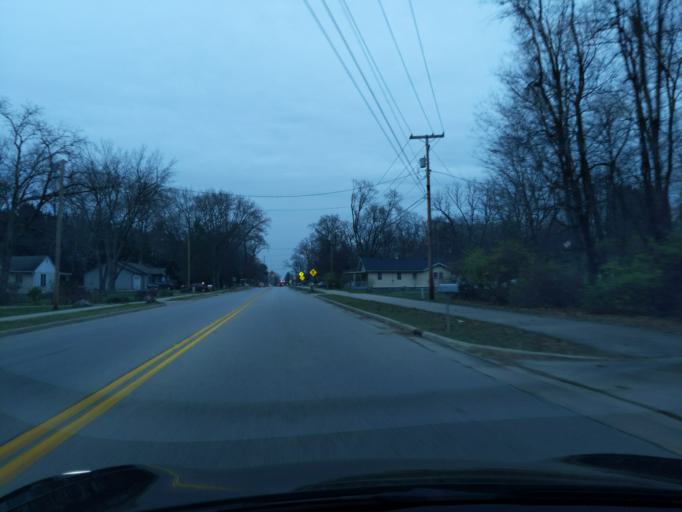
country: US
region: Indiana
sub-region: Saint Joseph County
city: Georgetown
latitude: 41.7304
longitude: -86.2577
